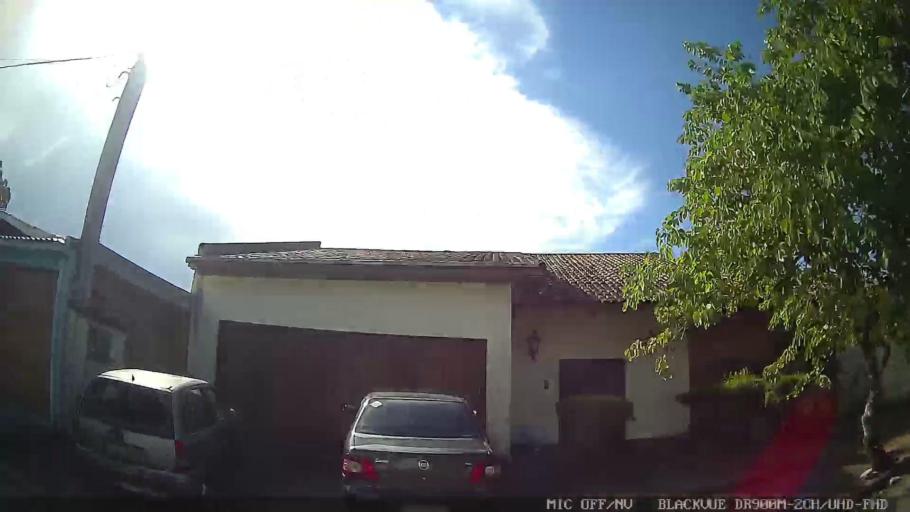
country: BR
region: Sao Paulo
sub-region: Iguape
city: Iguape
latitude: -24.7055
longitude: -47.5631
